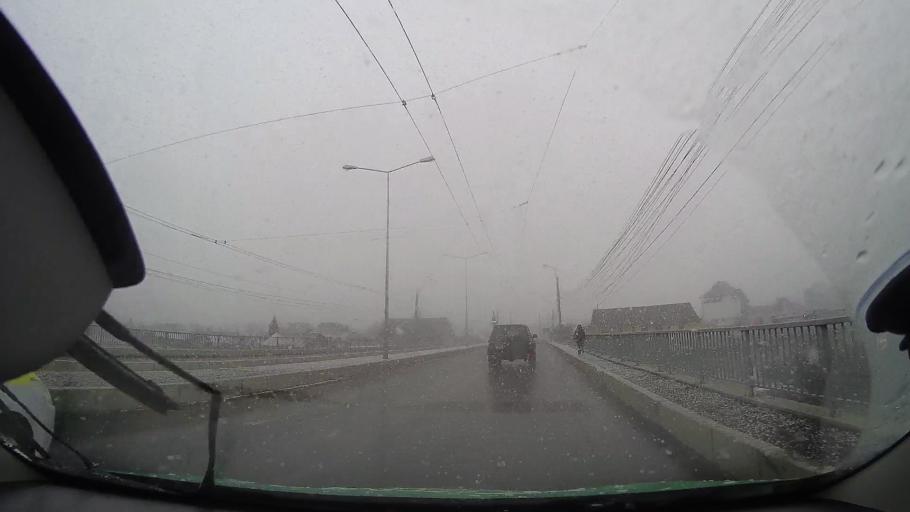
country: RO
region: Sibiu
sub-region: Municipiul Medias
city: Medias
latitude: 46.1711
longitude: 24.3461
